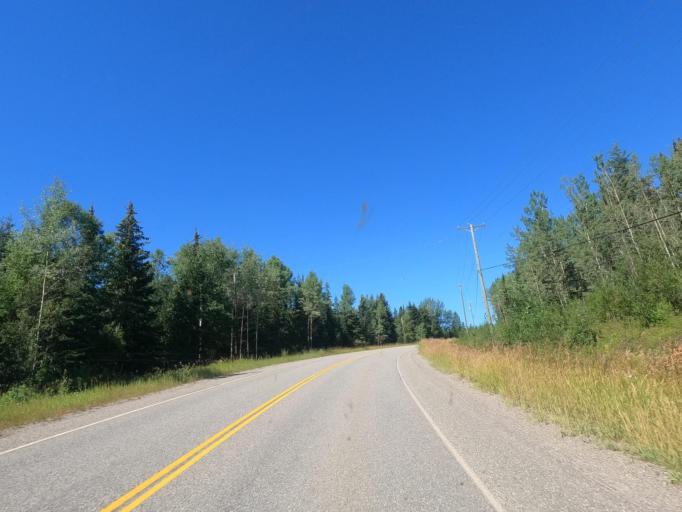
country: CA
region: British Columbia
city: Quesnel
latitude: 53.0225
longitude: -122.3714
